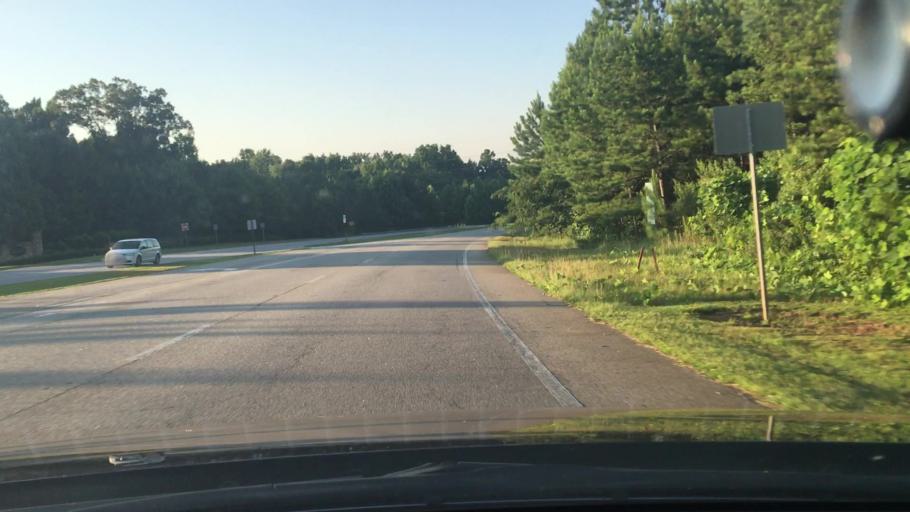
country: US
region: Georgia
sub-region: Coweta County
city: East Newnan
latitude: 33.3648
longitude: -84.7655
